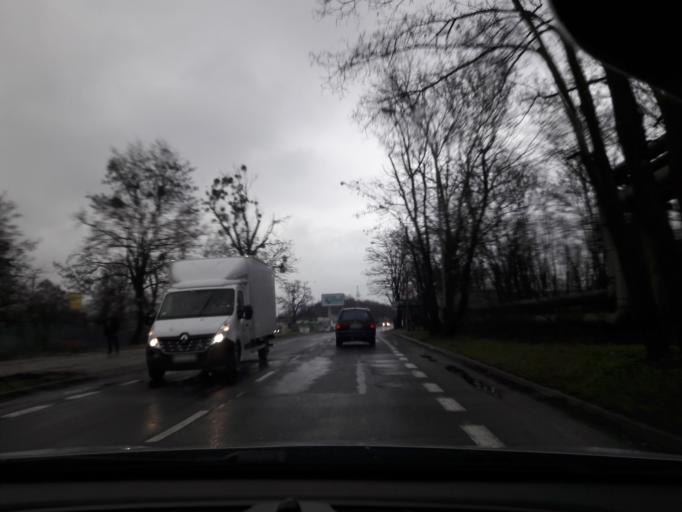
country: PL
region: Greater Poland Voivodeship
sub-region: Powiat poznanski
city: Suchy Las
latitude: 52.4441
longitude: 16.9025
